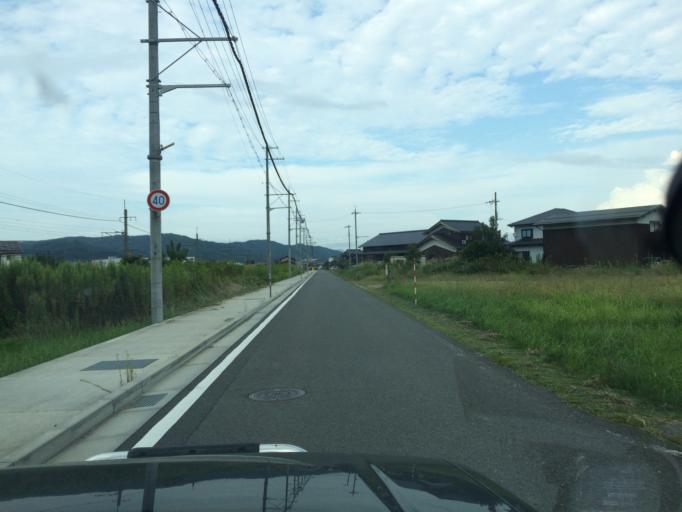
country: JP
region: Hyogo
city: Toyooka
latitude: 35.4753
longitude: 134.7810
